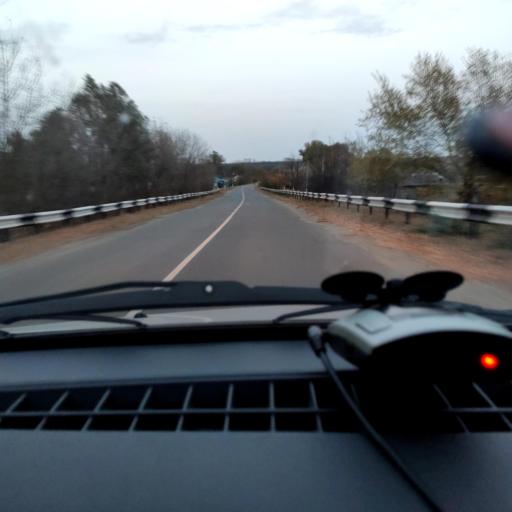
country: RU
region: Voronezj
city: Uryv-Pokrovka
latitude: 51.2309
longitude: 38.9259
